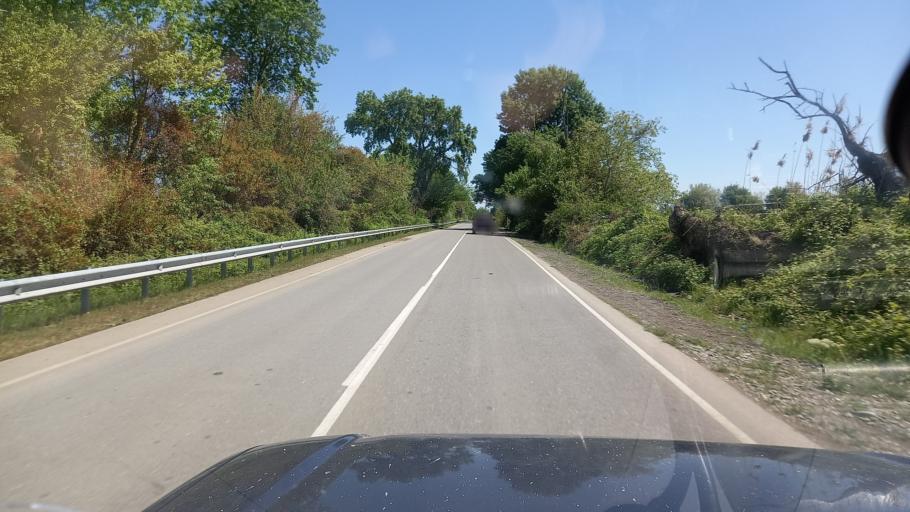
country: RU
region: Dagestan
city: Samur
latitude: 41.7373
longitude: 48.4760
